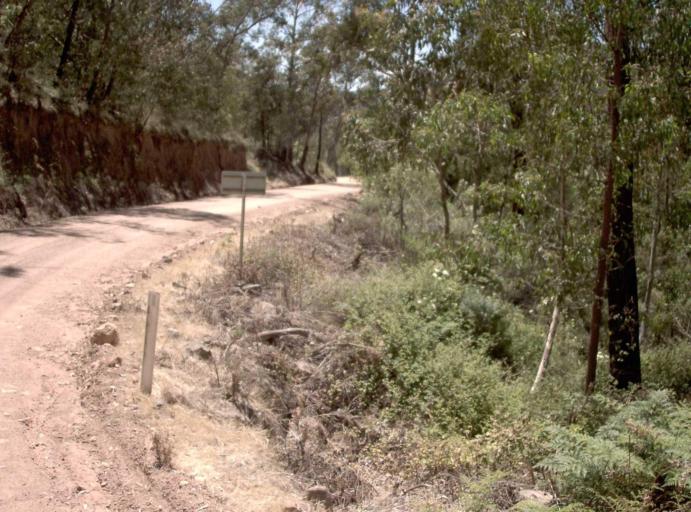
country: AU
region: New South Wales
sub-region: Snowy River
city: Jindabyne
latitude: -36.9769
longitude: 148.3002
